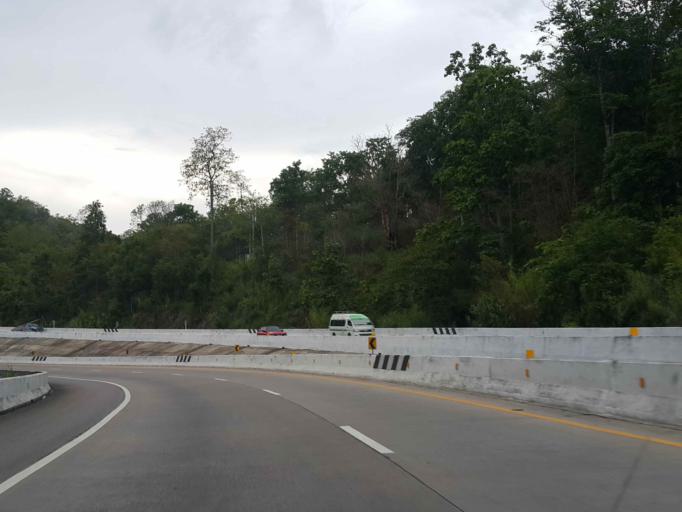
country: TH
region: Lampang
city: Hang Chat
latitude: 18.3774
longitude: 99.2324
